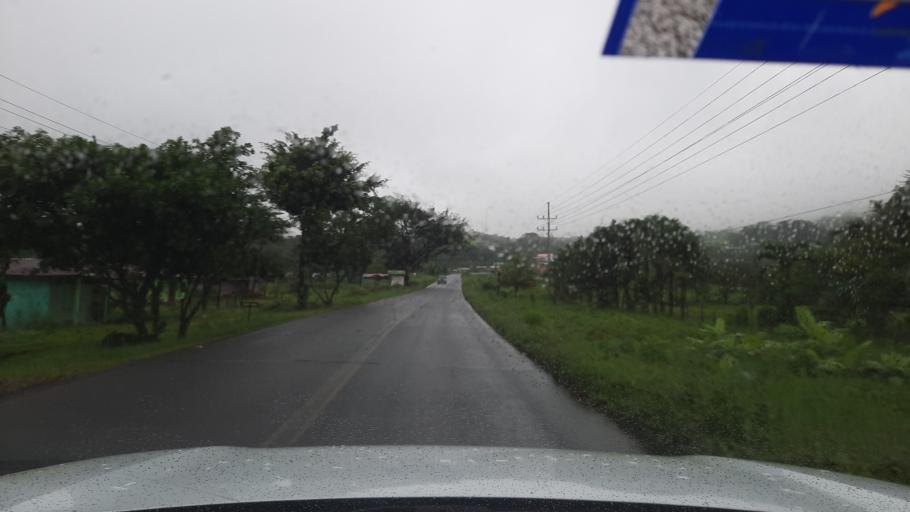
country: CR
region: Alajuela
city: Bijagua
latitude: 10.7208
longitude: -85.0686
